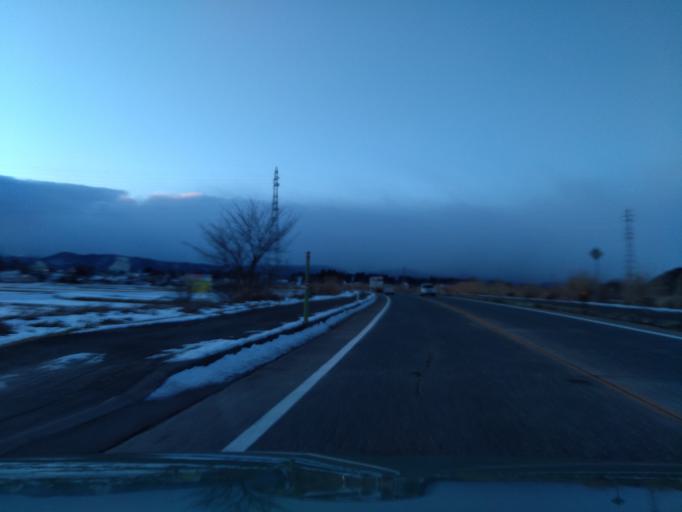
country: JP
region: Iwate
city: Shizukuishi
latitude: 39.7012
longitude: 140.9748
